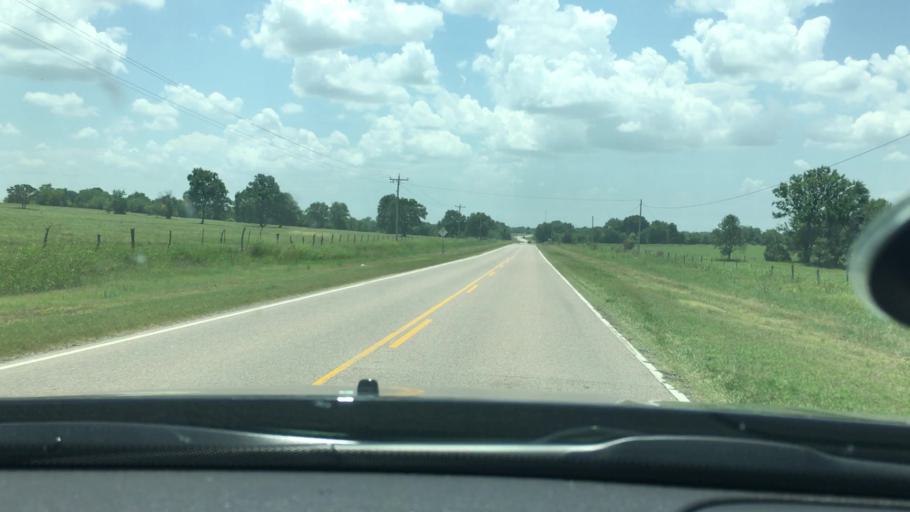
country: US
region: Oklahoma
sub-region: Johnston County
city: Tishomingo
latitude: 34.4690
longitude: -96.6360
